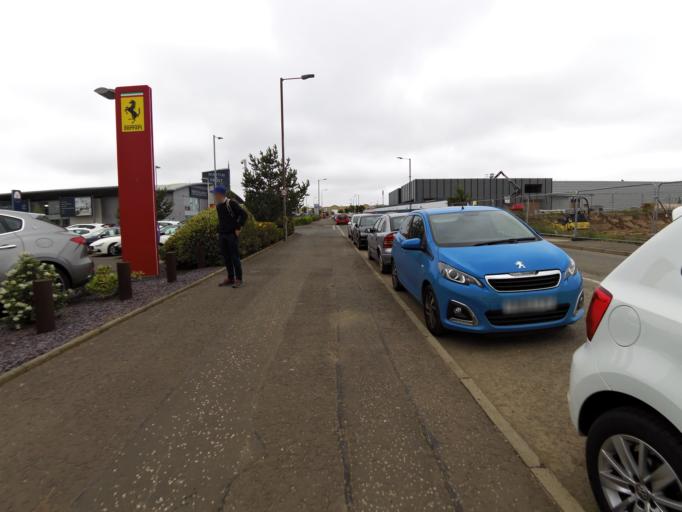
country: GB
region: Scotland
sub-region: Midlothian
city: Dalkeith
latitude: 55.9307
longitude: -3.1046
